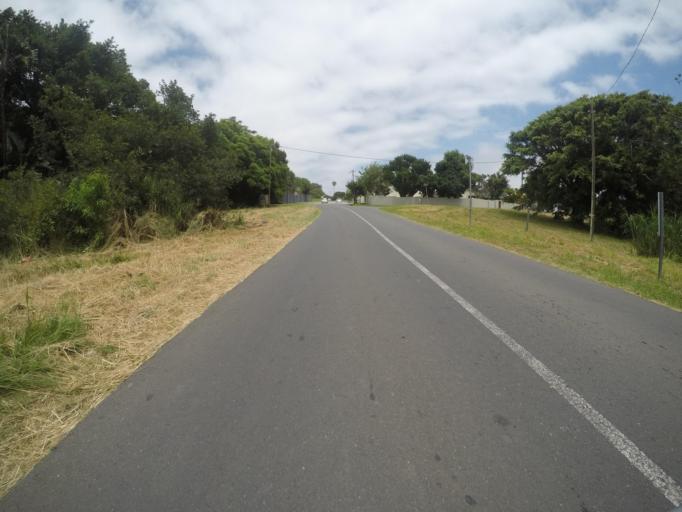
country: ZA
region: Eastern Cape
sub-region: Buffalo City Metropolitan Municipality
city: East London
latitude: -32.9910
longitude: 27.9306
